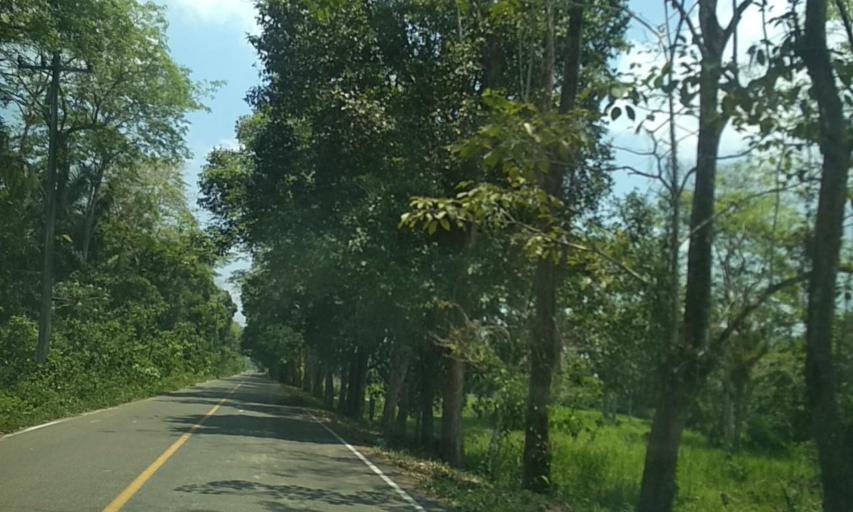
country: MX
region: Tabasco
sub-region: Huimanguillo
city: Francisco Rueda
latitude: 17.7555
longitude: -94.0283
